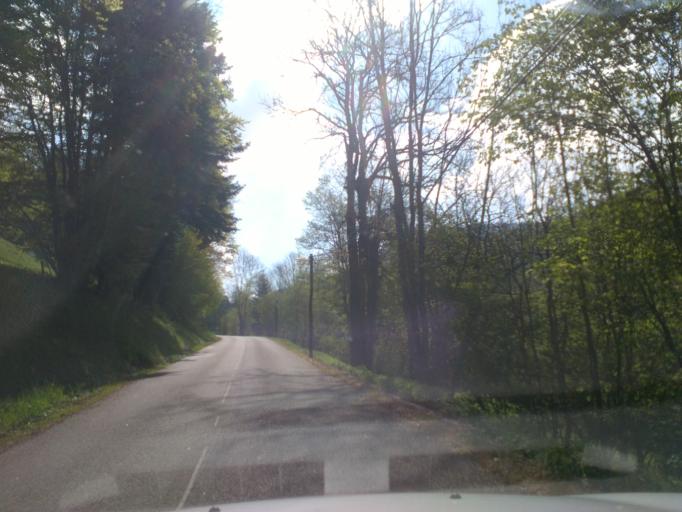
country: FR
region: Lorraine
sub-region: Departement des Vosges
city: Saulxures-sur-Moselotte
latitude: 47.9892
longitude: 6.7734
